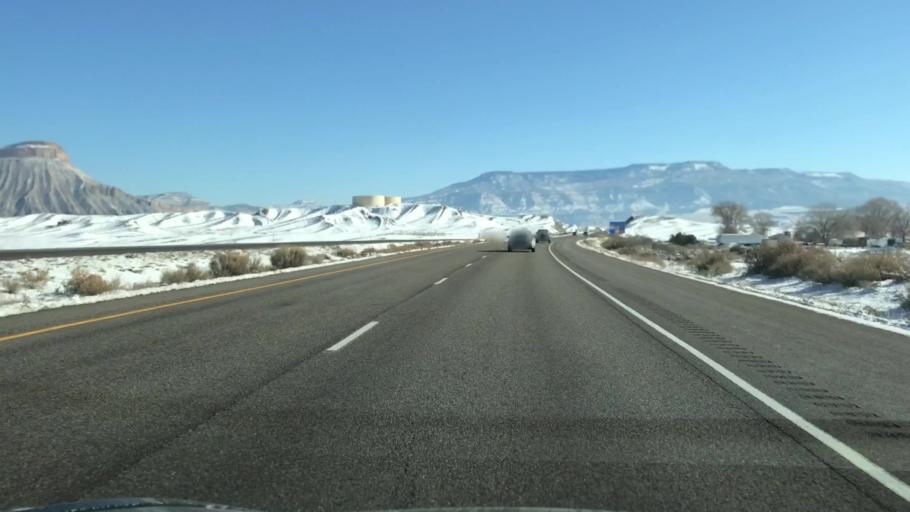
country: US
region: Colorado
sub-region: Mesa County
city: Clifton
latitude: 39.1047
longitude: -108.4725
